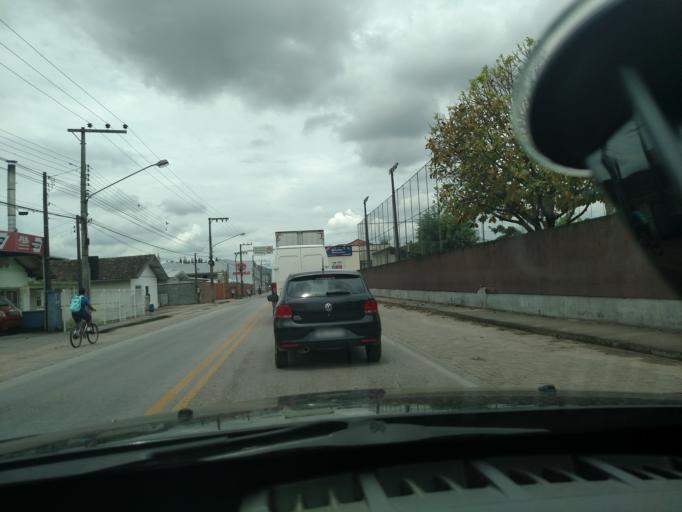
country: BR
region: Santa Catarina
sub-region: Gaspar
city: Gaspar
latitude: -26.9266
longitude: -48.9656
